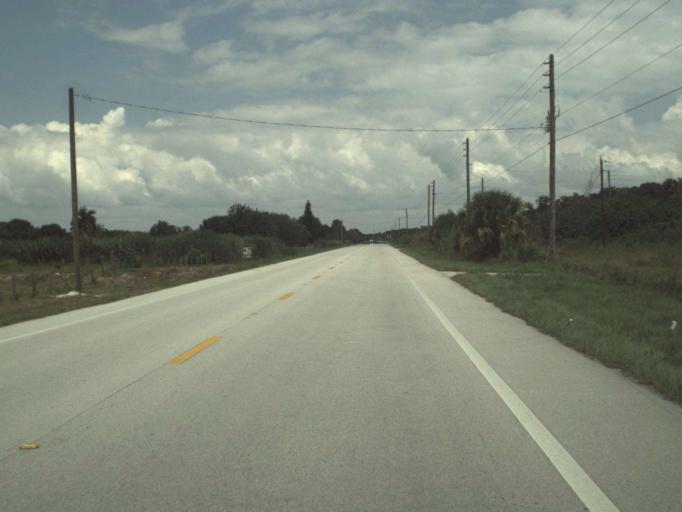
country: US
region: Florida
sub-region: Okeechobee County
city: Taylor Creek
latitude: 27.1133
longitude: -80.6662
